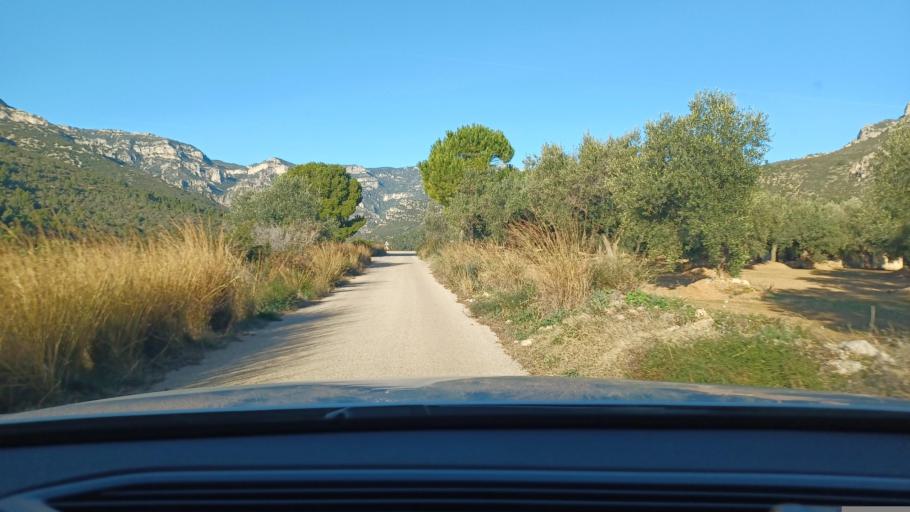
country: ES
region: Catalonia
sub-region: Provincia de Tarragona
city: Mas de Barberans
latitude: 40.7178
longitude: 0.3526
